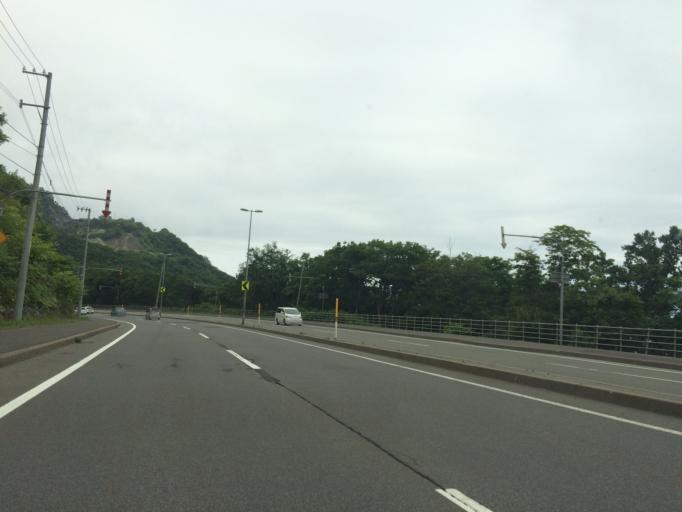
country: JP
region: Hokkaido
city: Otaru
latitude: 43.1622
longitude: 141.1061
